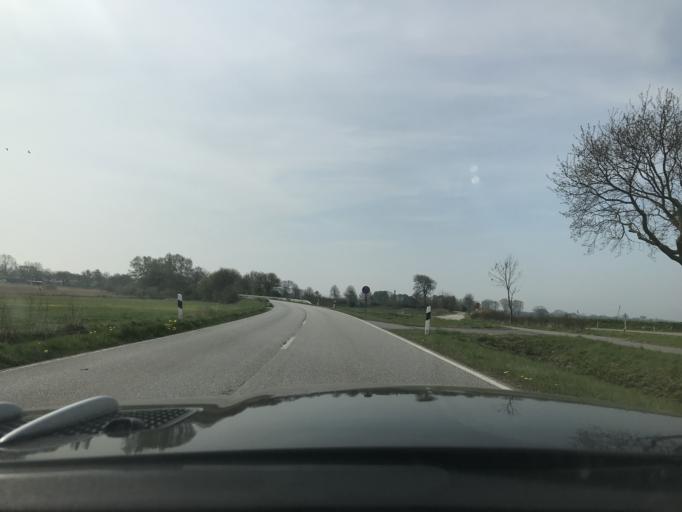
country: DE
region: Schleswig-Holstein
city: Grube
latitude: 54.2451
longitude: 11.0308
